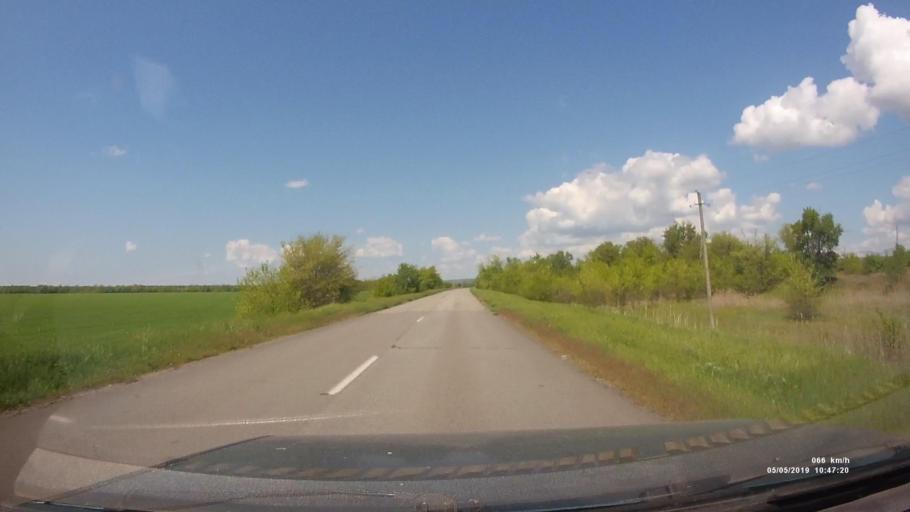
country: RU
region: Rostov
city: Ust'-Donetskiy
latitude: 47.6381
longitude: 40.8341
